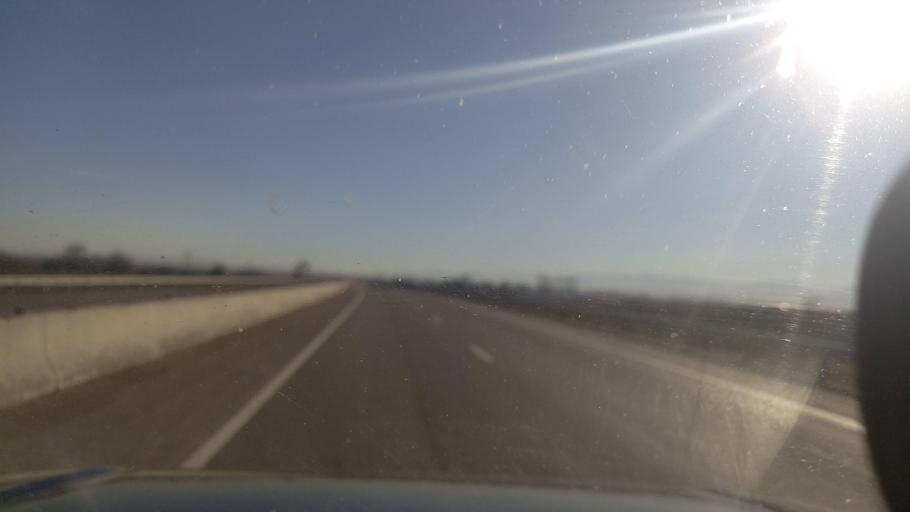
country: RU
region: Kabardino-Balkariya
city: Kishpek
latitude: 43.5921
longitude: 43.6727
